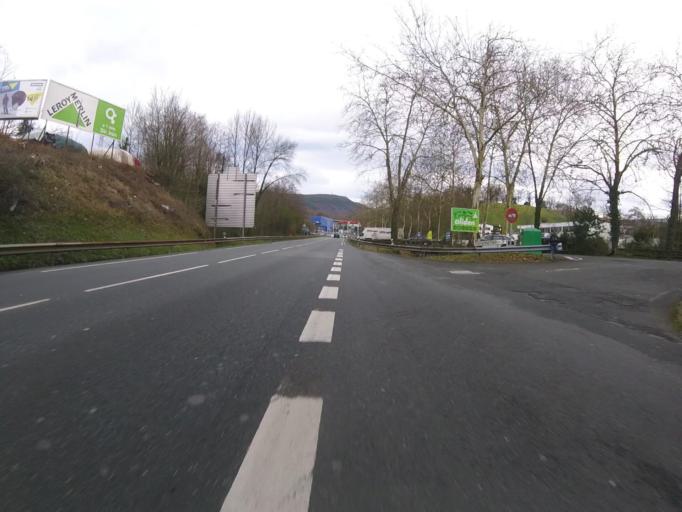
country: ES
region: Basque Country
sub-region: Provincia de Guipuzcoa
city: Lezo
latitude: 43.3154
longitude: -1.8749
